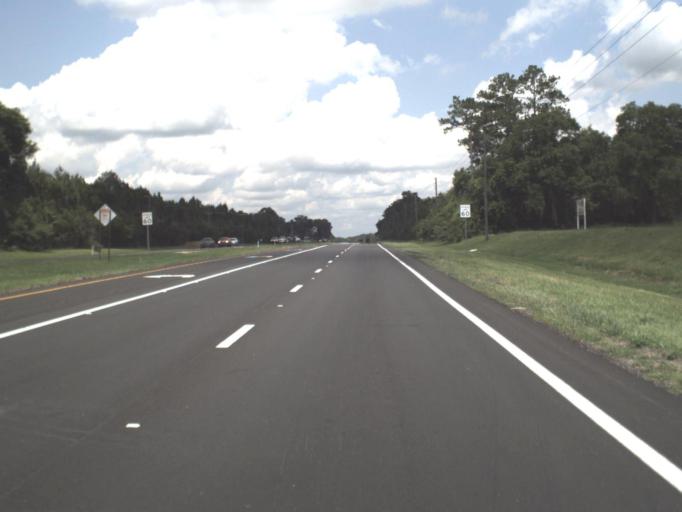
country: US
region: Florida
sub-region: Alachua County
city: Alachua
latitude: 29.7666
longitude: -82.4139
